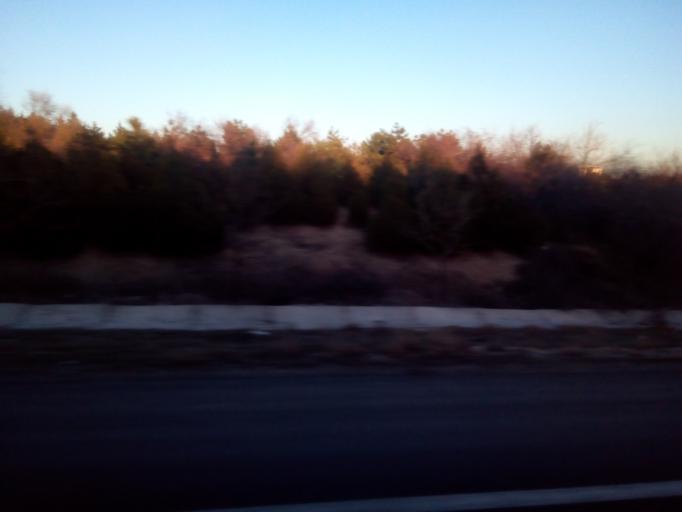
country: TR
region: Ankara
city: Etimesgut
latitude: 40.0183
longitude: 32.6248
